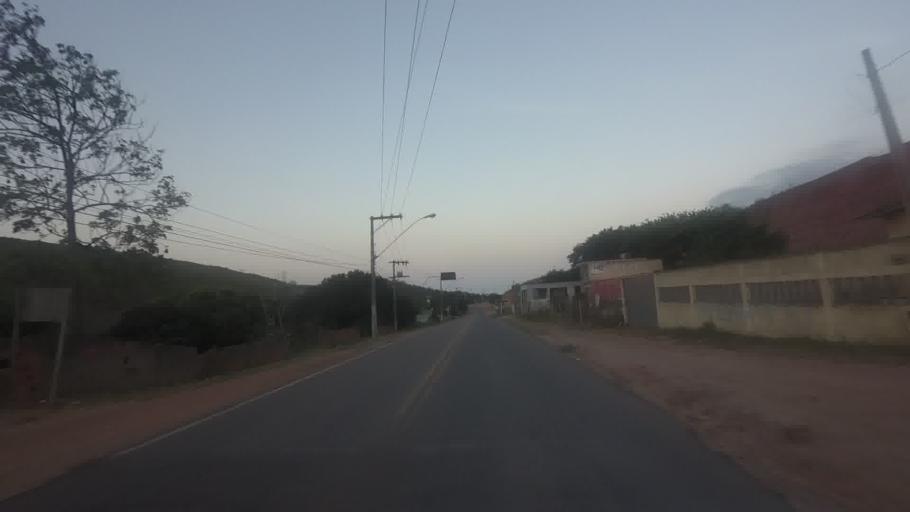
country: BR
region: Espirito Santo
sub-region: Piuma
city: Piuma
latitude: -20.8879
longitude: -40.7699
